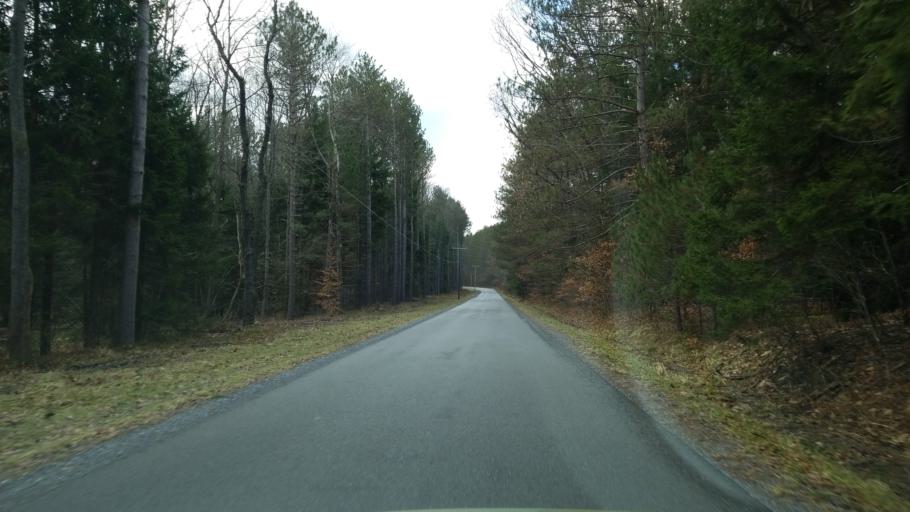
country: US
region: Pennsylvania
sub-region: Clearfield County
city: Treasure Lake
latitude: 41.1470
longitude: -78.5534
